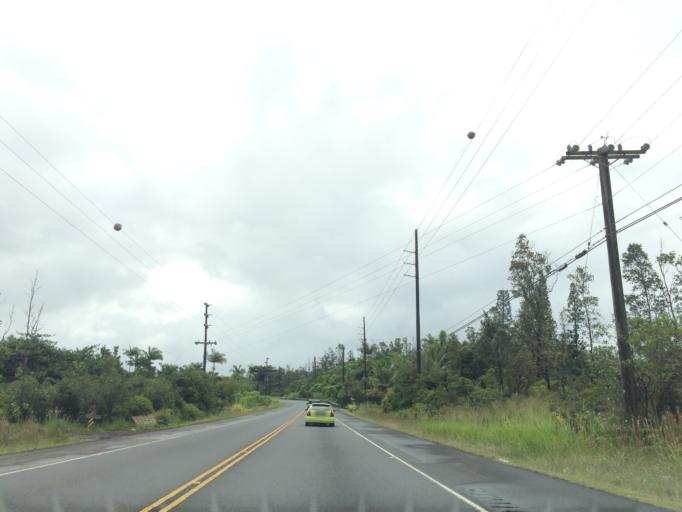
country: US
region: Hawaii
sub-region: Hawaii County
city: Hawaiian Paradise Park
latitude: 19.5145
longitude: -154.9637
